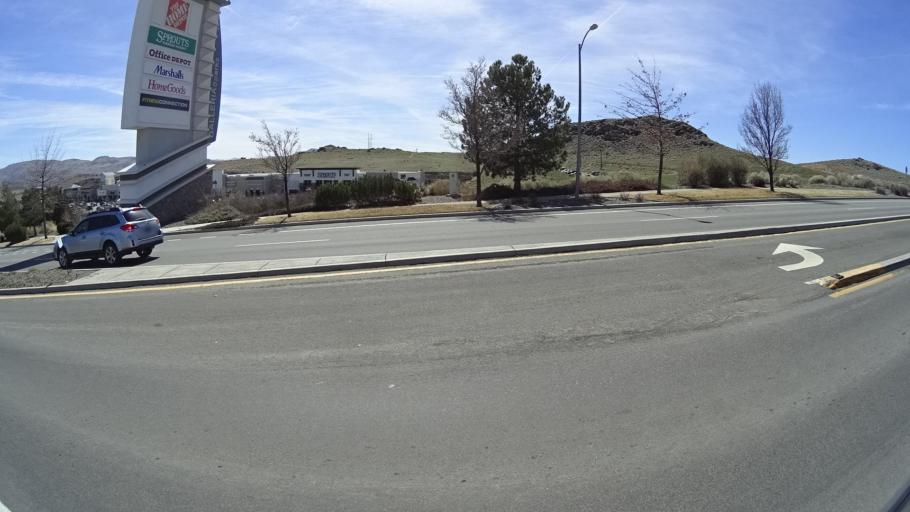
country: US
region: Nevada
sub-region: Washoe County
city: Sun Valley
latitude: 39.5766
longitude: -119.7433
